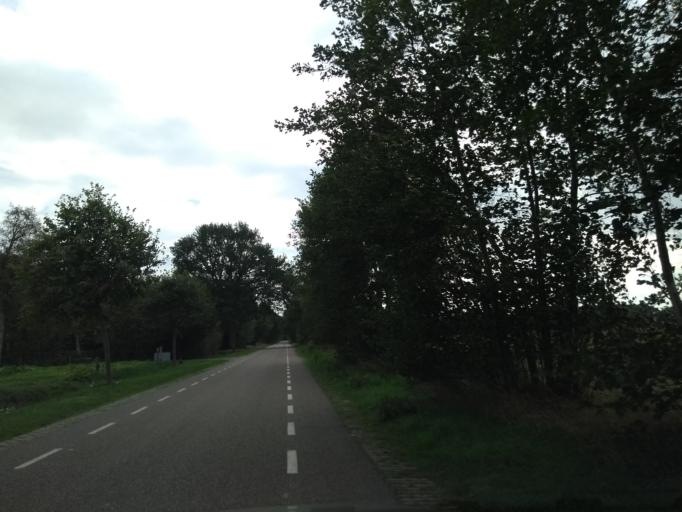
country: NL
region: Overijssel
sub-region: Gemeente Haaksbergen
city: Haaksbergen
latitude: 52.1388
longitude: 6.7464
